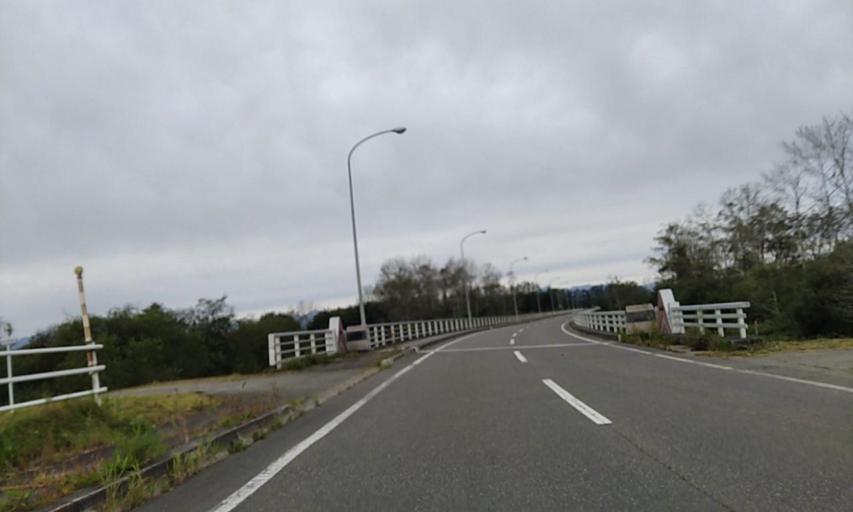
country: JP
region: Hokkaido
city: Obihiro
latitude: 42.7199
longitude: 143.1445
